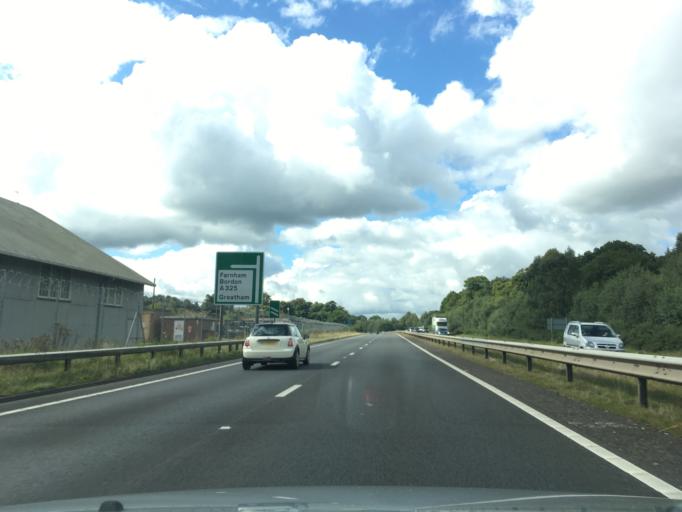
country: GB
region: England
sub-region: Hampshire
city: Bordon
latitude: 51.0748
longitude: -0.8652
